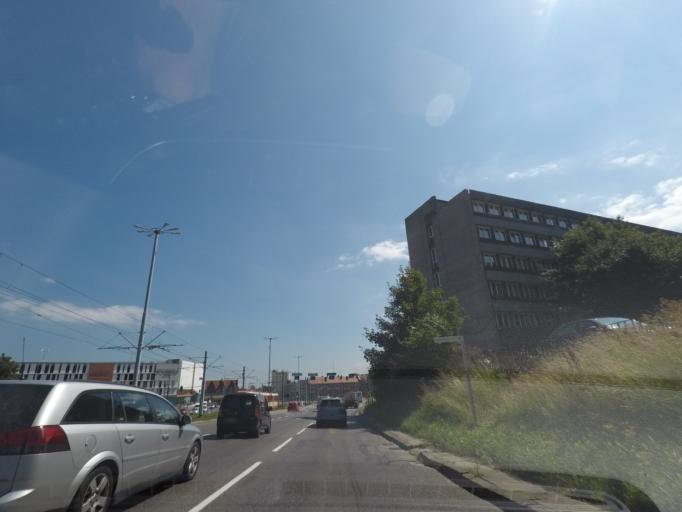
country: PL
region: Pomeranian Voivodeship
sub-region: Gdansk
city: Gdansk
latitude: 54.3483
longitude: 18.6400
